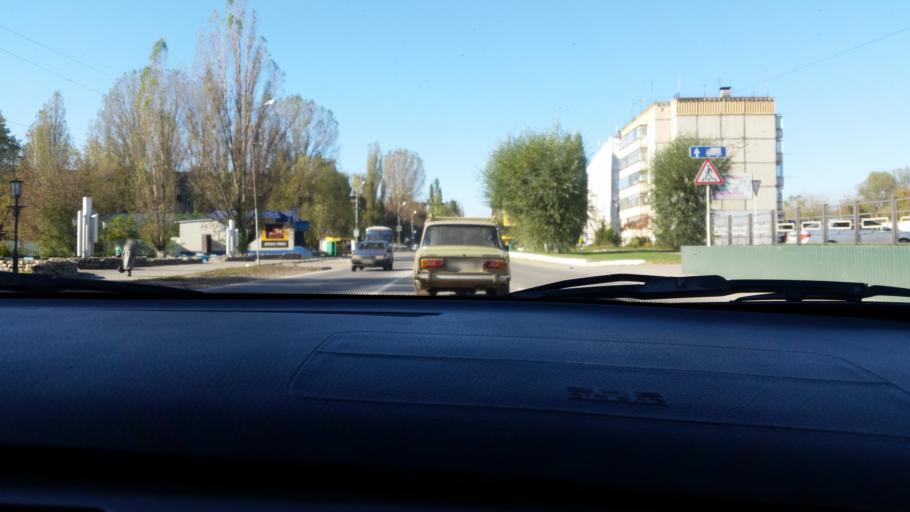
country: RU
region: Lipetsk
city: Gryazi
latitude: 52.4910
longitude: 39.9638
